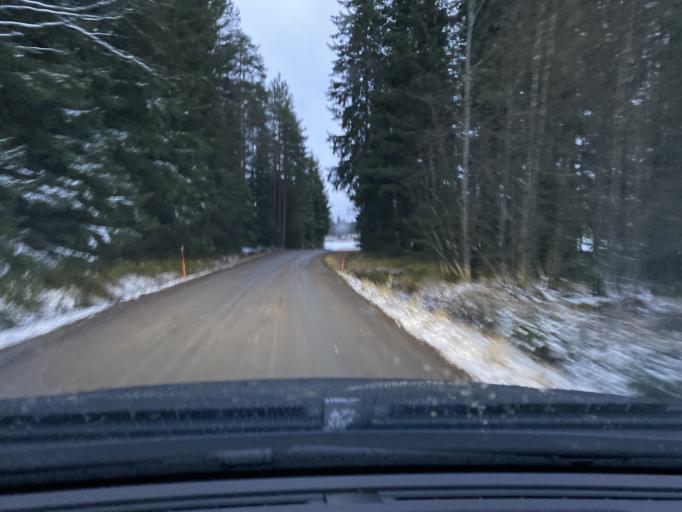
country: FI
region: Pirkanmaa
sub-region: Lounais-Pirkanmaa
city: Punkalaidun
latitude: 61.1622
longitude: 22.9459
